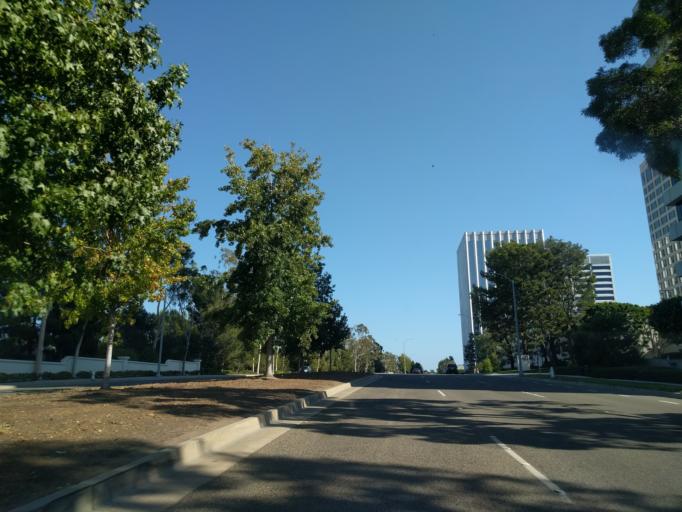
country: US
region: California
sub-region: Orange County
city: San Joaquin Hills
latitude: 33.6217
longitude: -117.8743
